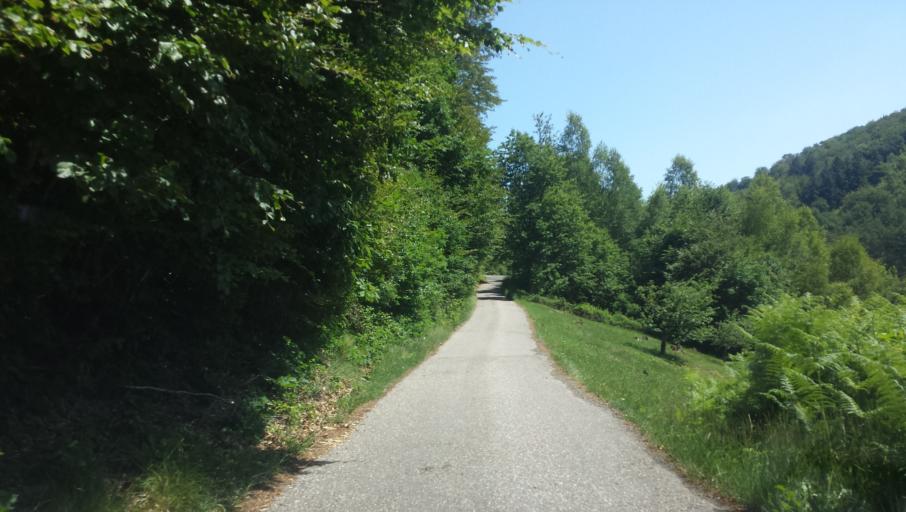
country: DE
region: Rheinland-Pfalz
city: Trippstadt
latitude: 49.3413
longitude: 7.8365
